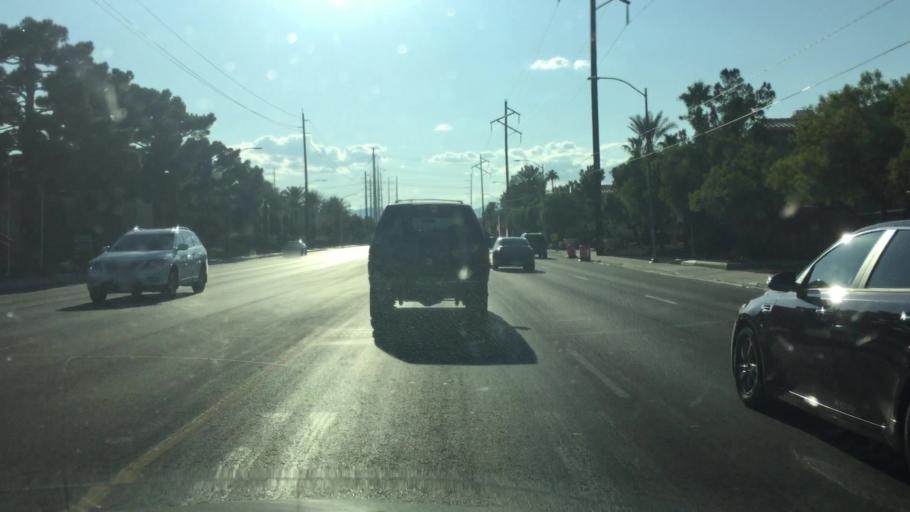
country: US
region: Nevada
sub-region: Clark County
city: Spring Valley
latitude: 36.1591
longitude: -115.2742
